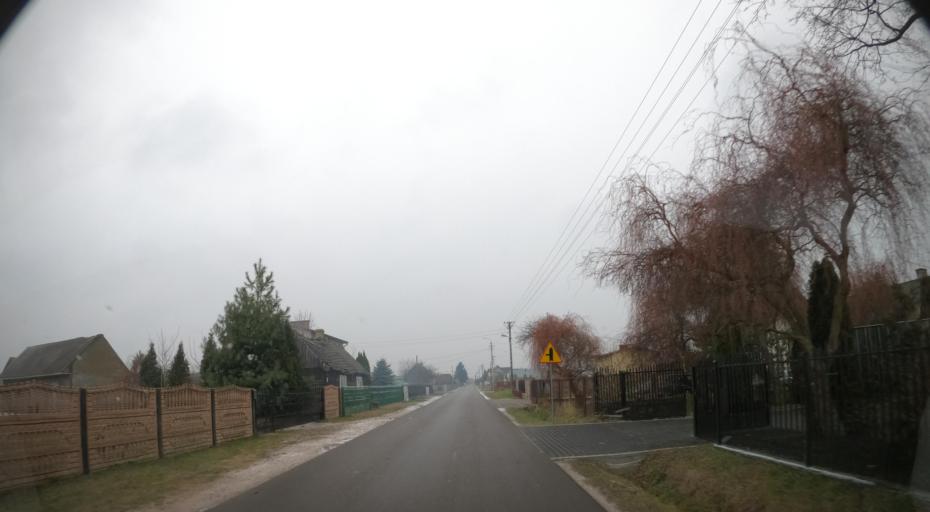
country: PL
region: Masovian Voivodeship
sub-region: Powiat radomski
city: Jedlnia-Letnisko
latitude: 51.3934
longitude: 21.2640
